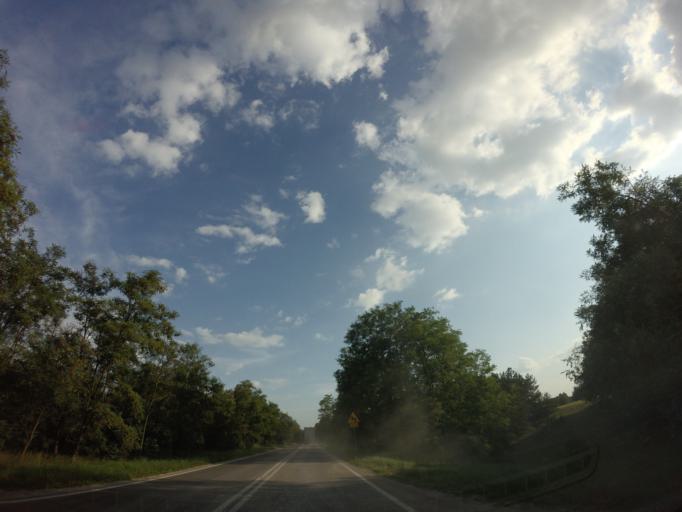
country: PL
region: Lublin Voivodeship
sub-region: Powiat lubartowski
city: Jeziorzany
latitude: 51.5836
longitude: 22.2823
